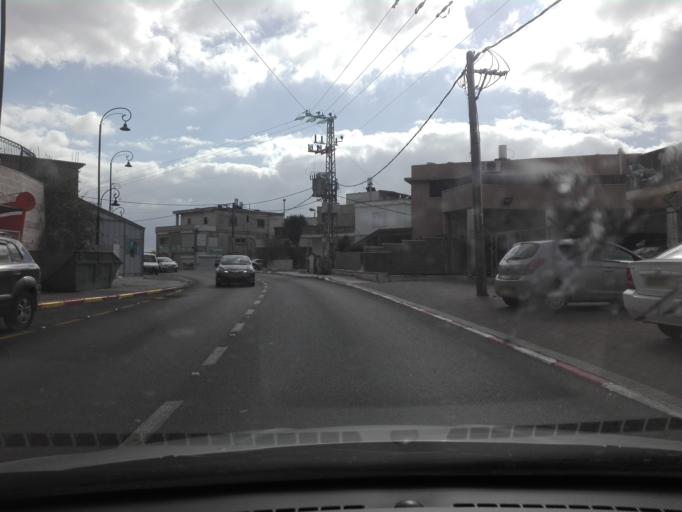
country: IL
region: Haifa
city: Daliyat el Karmil
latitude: 32.7175
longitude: 35.0654
